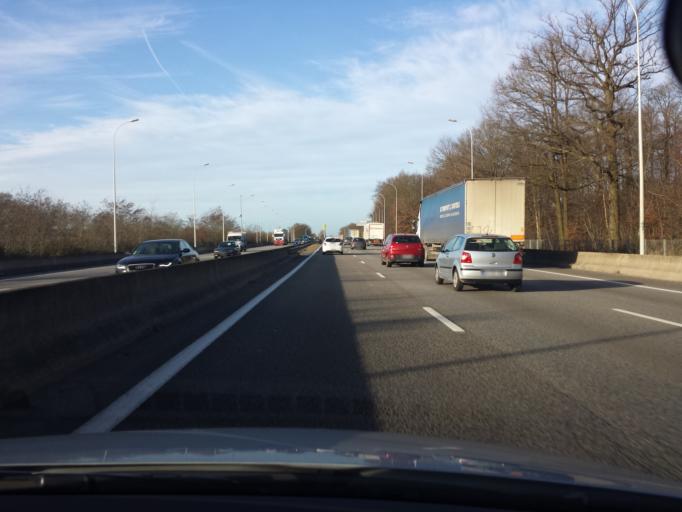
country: FR
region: Ile-de-France
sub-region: Departement des Yvelines
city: Saint-Cyr-l'Ecole
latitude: 48.7928
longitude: 2.0871
